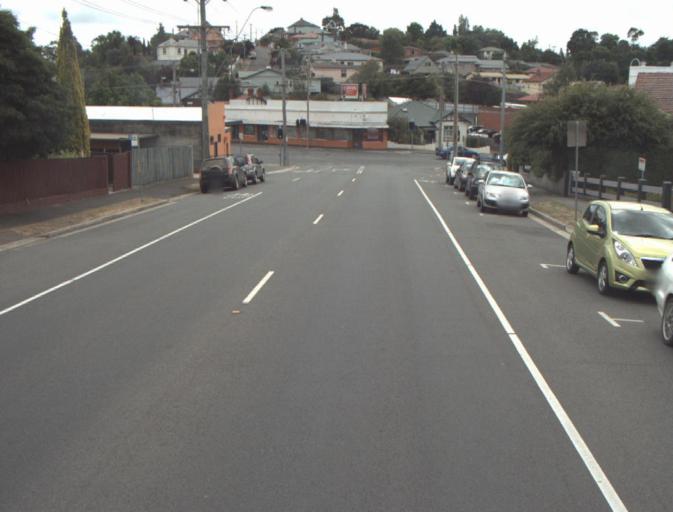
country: AU
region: Tasmania
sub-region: Launceston
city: East Launceston
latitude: -41.4595
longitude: 147.1531
